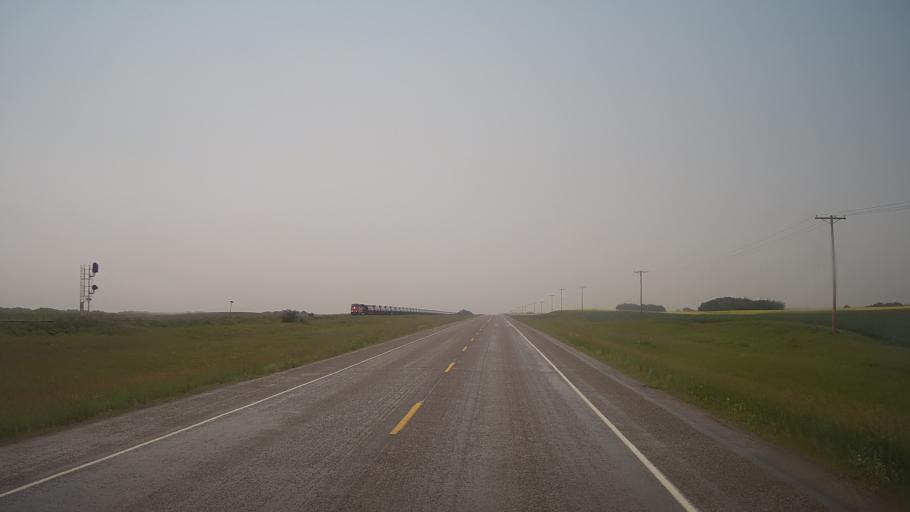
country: CA
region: Saskatchewan
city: Biggar
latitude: 52.1567
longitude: -108.2602
